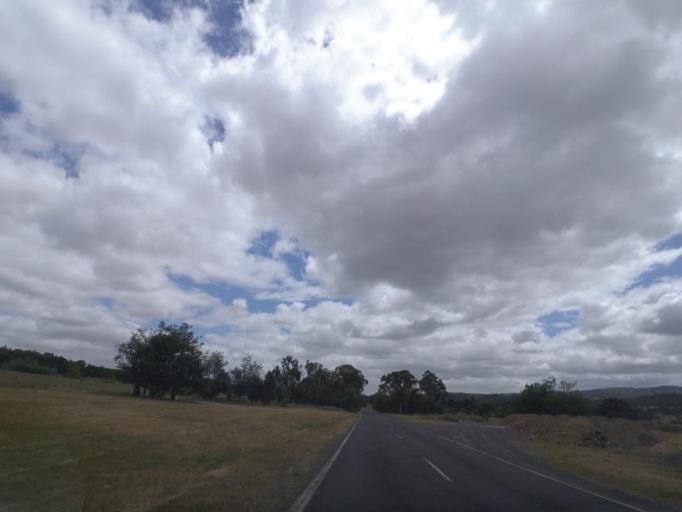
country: AU
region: Victoria
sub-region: Whittlesea
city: Whittlesea
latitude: -37.2966
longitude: 145.0572
